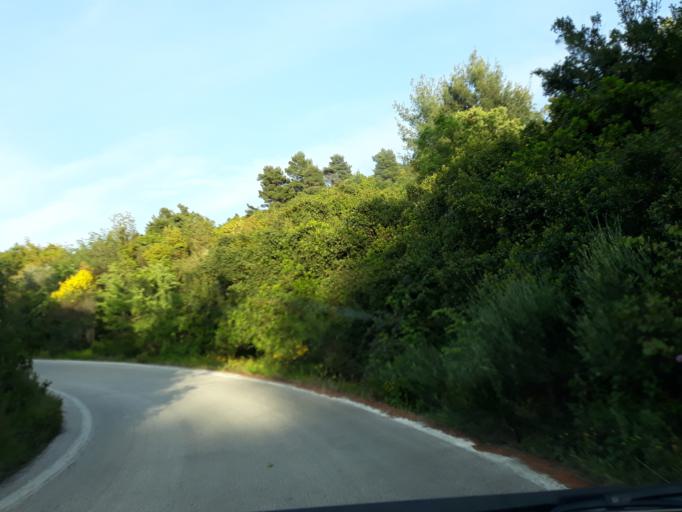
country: GR
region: Attica
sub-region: Nomarchia Anatolikis Attikis
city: Afidnes
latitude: 38.2271
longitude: 23.7897
